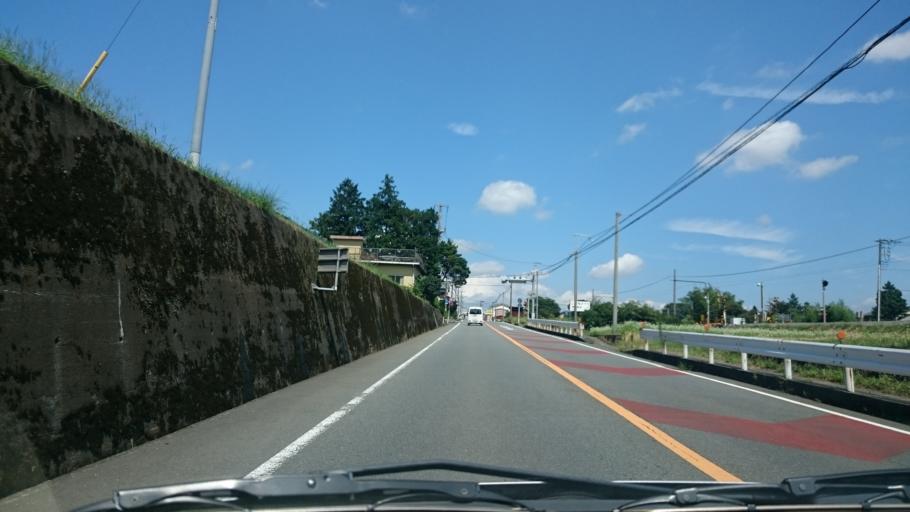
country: JP
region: Shizuoka
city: Gotemba
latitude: 35.2732
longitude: 138.9238
